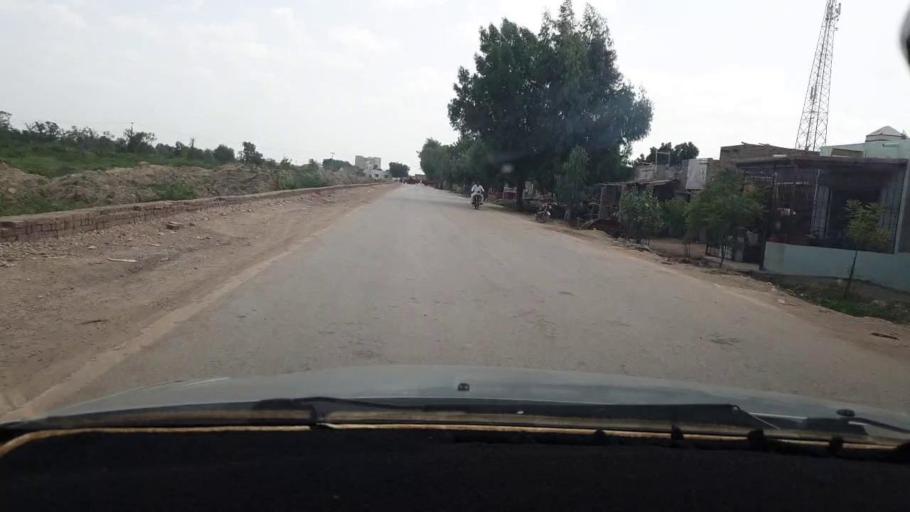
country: PK
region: Sindh
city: Digri
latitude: 25.0654
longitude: 69.2178
